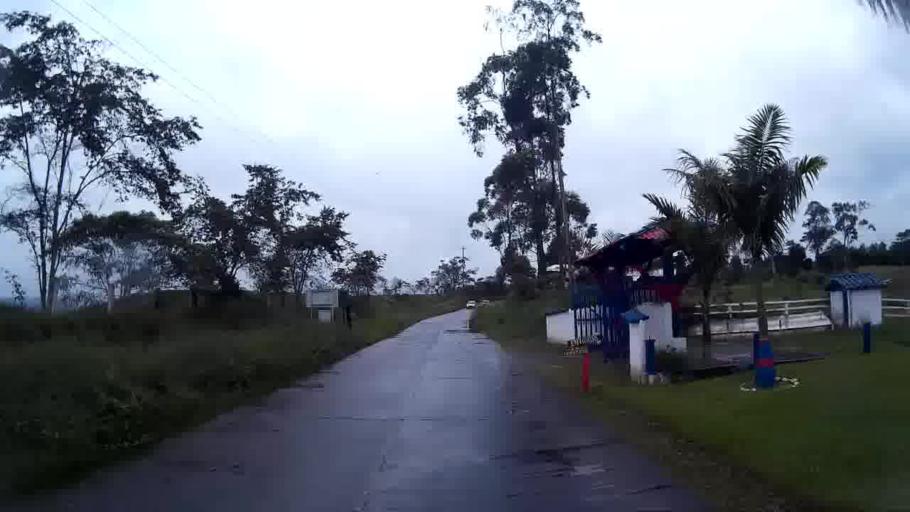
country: CO
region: Quindio
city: Filandia
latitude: 4.6884
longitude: -75.6323
